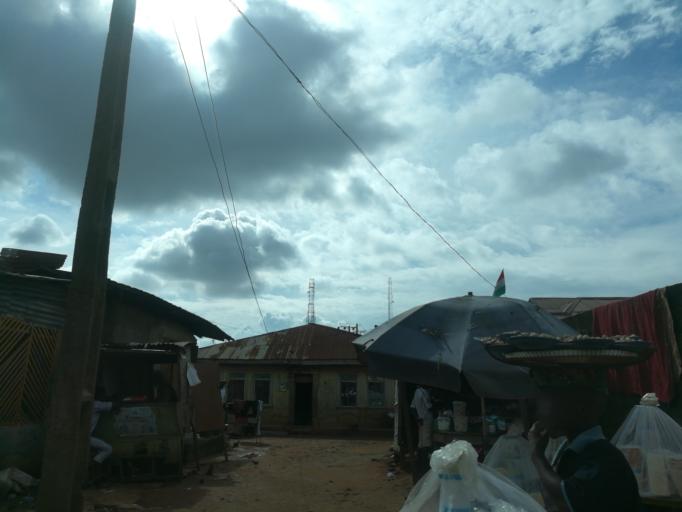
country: NG
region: Lagos
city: Ikorodu
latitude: 6.5932
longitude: 3.5168
